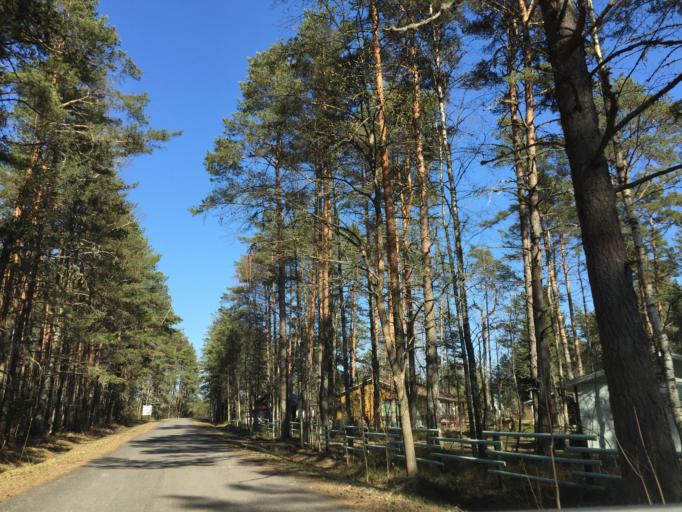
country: EE
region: Jogevamaa
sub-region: Mustvee linn
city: Mustvee
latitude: 58.9941
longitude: 27.2597
